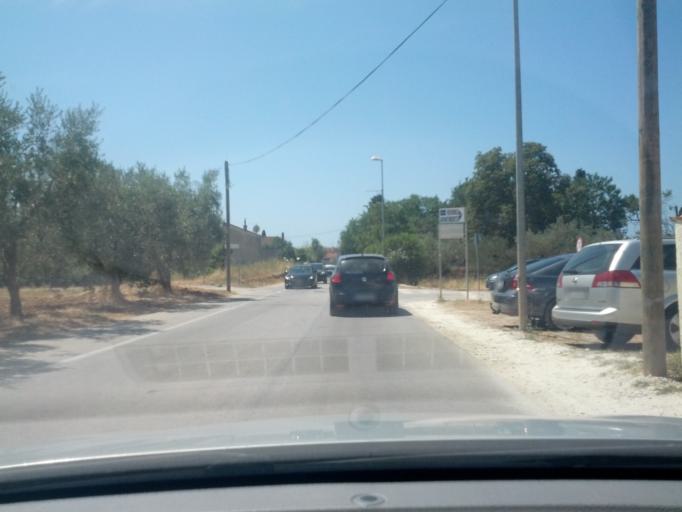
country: HR
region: Istarska
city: Fazana
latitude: 44.9312
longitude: 13.8054
